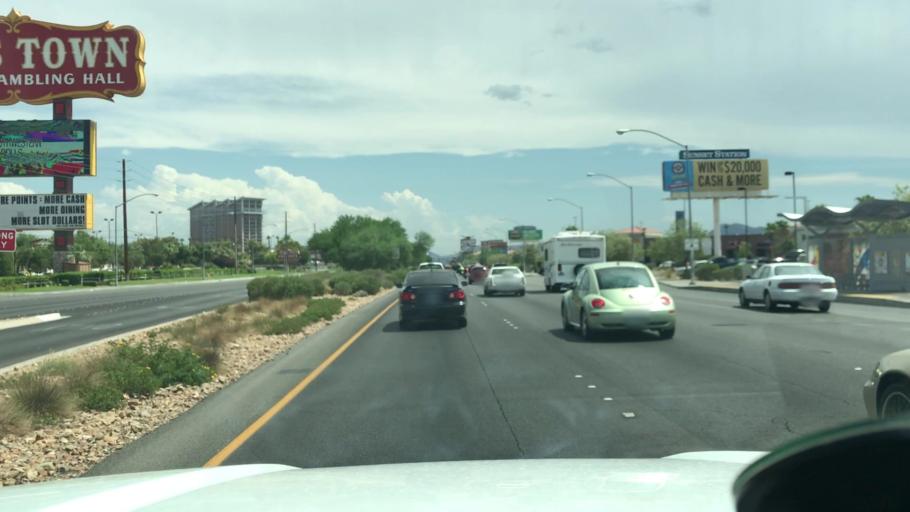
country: US
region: Nevada
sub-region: Clark County
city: Whitney
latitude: 36.1125
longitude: -115.0642
